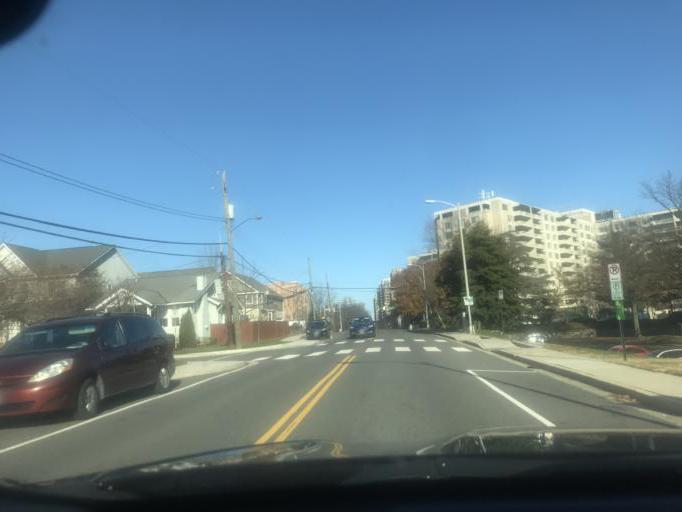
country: US
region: Washington, D.C.
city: Washington, D.C.
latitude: 38.8561
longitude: -77.0553
